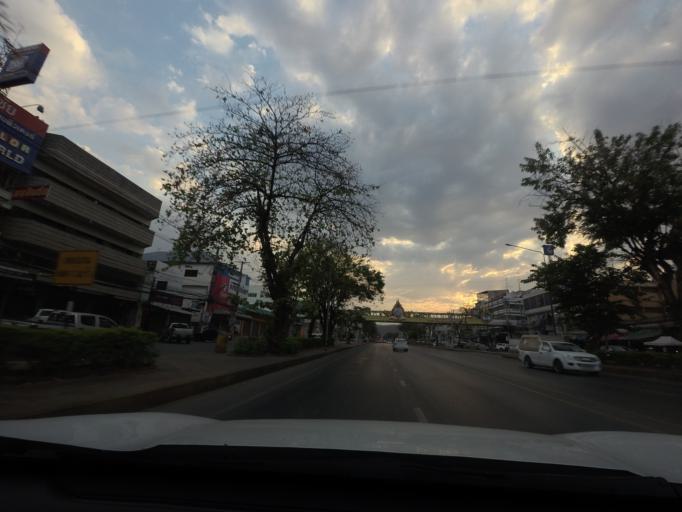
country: TH
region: Nakhon Ratchasima
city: Pak Chong
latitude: 14.7062
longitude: 101.4161
